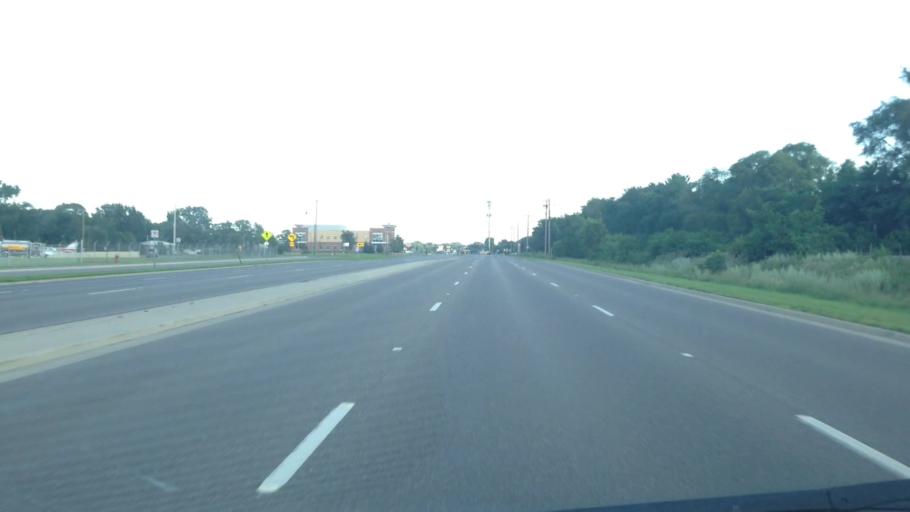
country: US
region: Minnesota
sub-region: Hennepin County
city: Crystal
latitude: 45.0598
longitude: -93.3619
